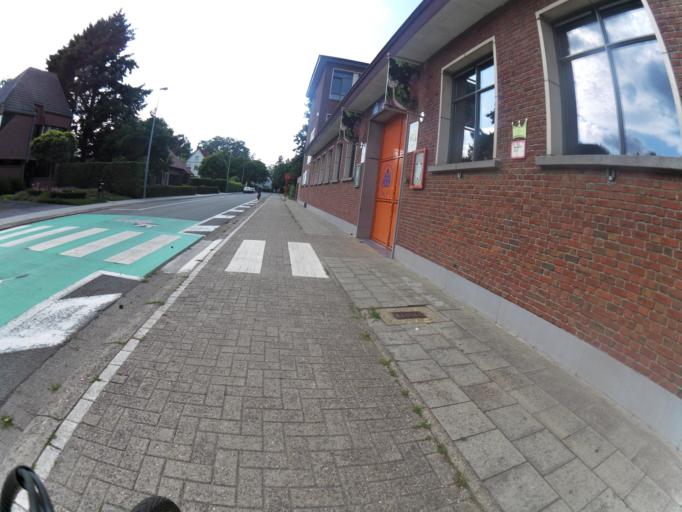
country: BE
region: Flanders
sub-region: Provincie Antwerpen
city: Mol
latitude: 51.1865
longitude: 5.1067
